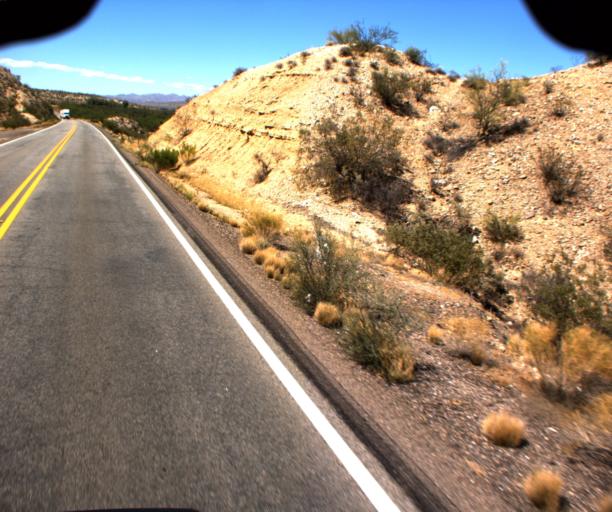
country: US
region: Arizona
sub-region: Yavapai County
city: Bagdad
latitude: 34.7795
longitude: -113.6226
